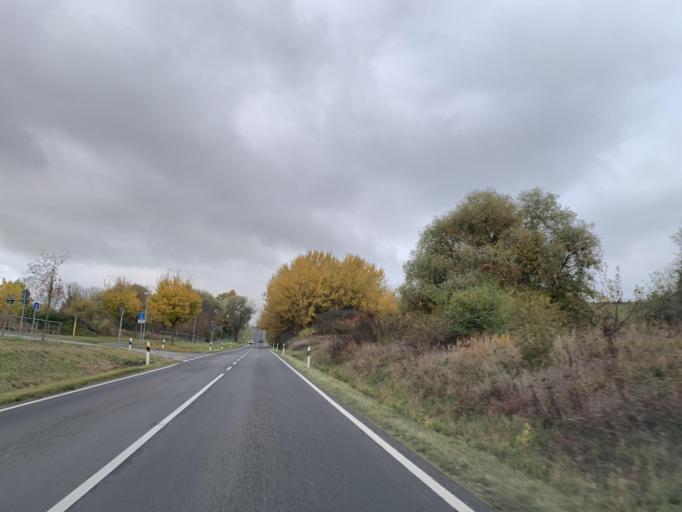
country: DE
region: Mecklenburg-Vorpommern
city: Trollenhagen
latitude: 53.5848
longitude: 13.2971
